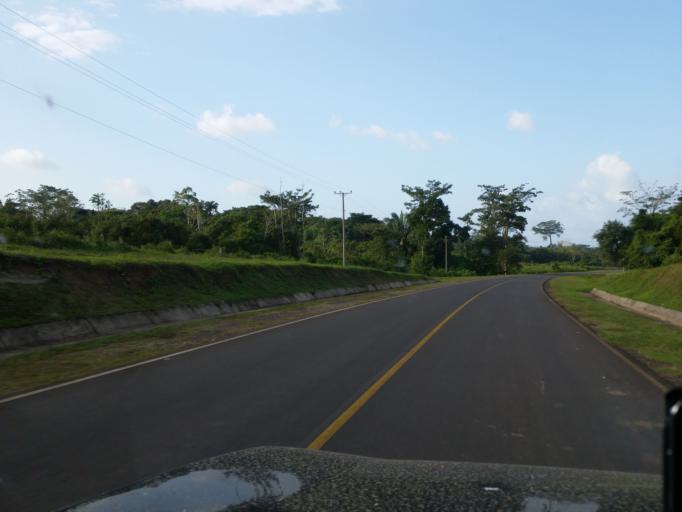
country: NI
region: Rio San Juan
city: San Carlos
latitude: 11.1777
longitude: -84.6781
